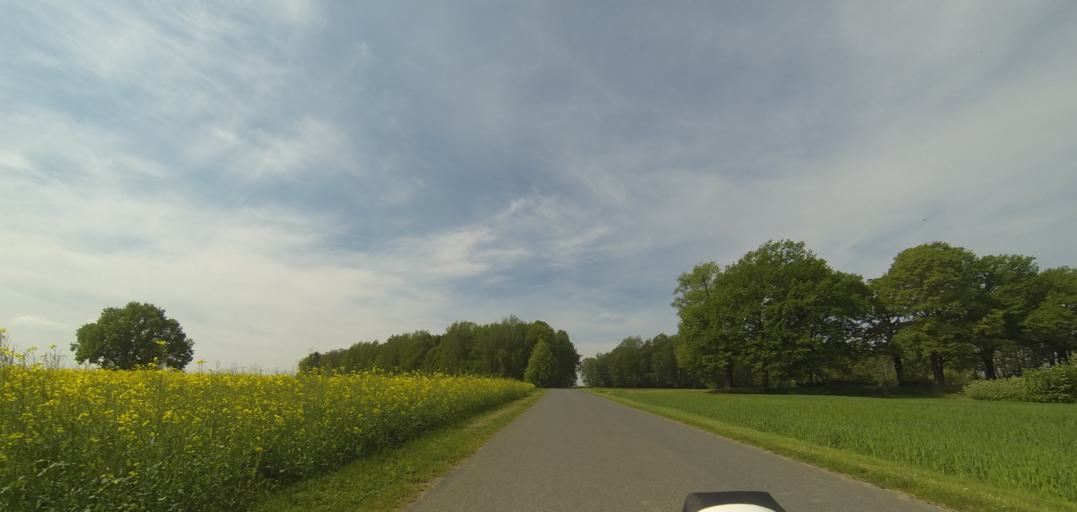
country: DE
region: Saxony
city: Arnsdorf
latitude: 51.0850
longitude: 13.9479
